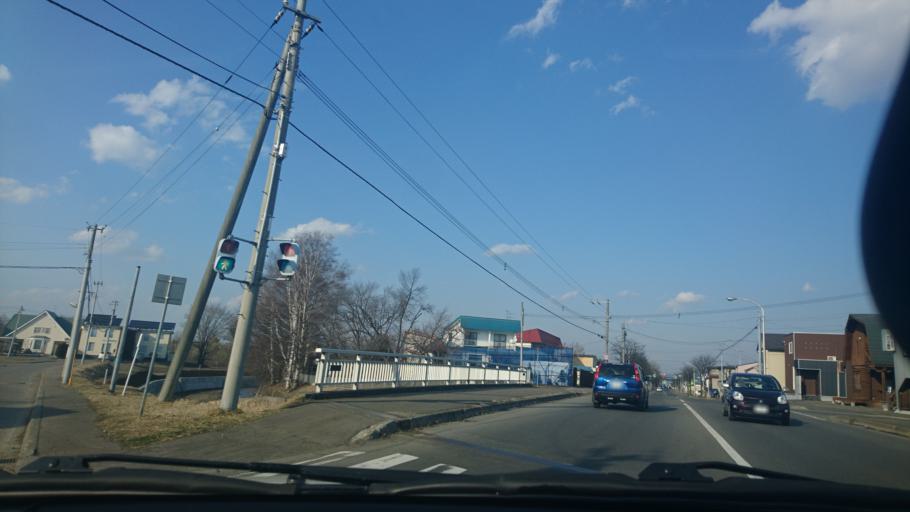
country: JP
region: Hokkaido
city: Obihiro
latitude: 42.9227
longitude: 143.1575
